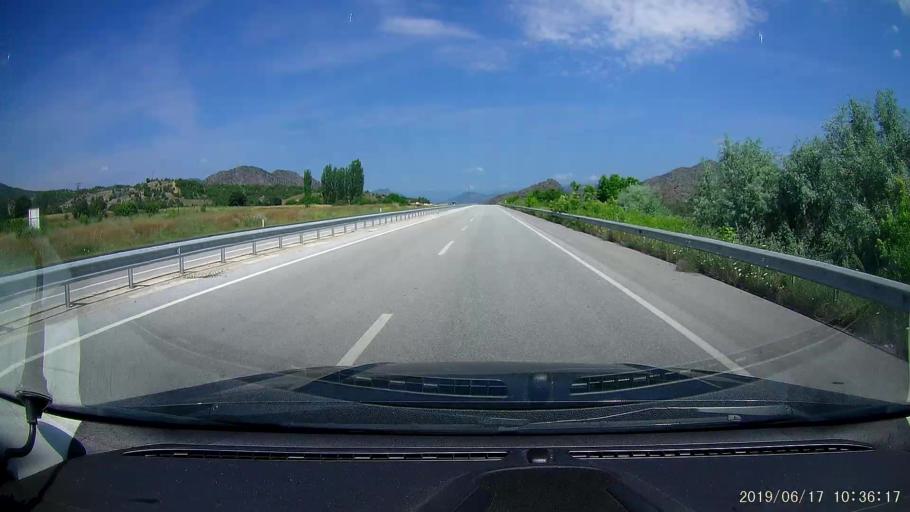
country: TR
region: Corum
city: Osmancik
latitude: 40.9772
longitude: 34.6843
